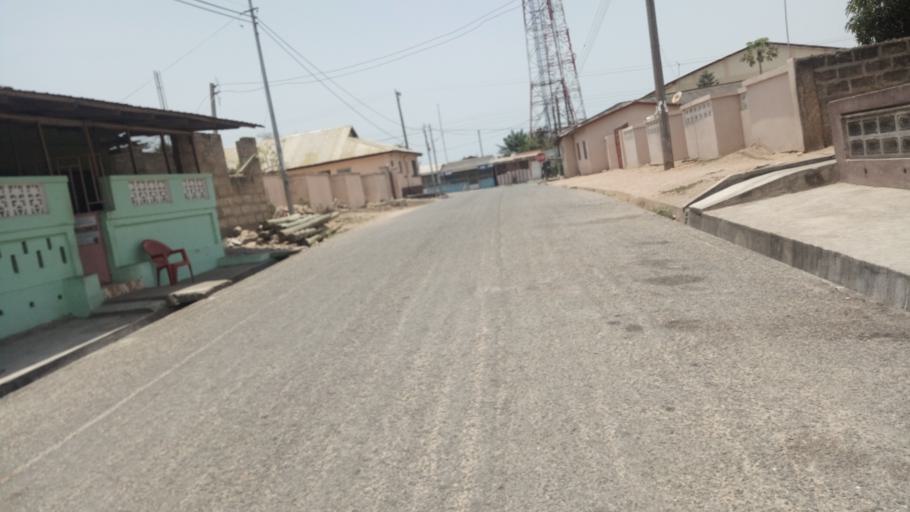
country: GH
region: Central
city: Winneba
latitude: 5.3447
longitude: -0.6247
